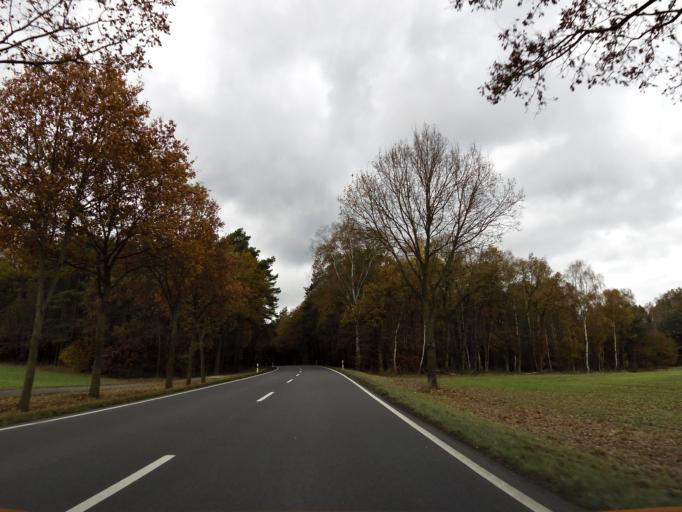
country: DE
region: Lower Saxony
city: Schnega
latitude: 52.9175
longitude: 10.8849
